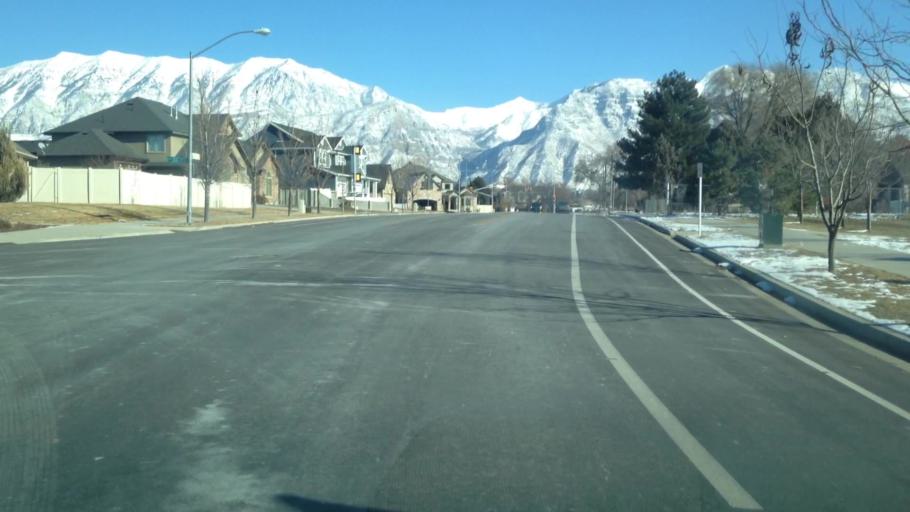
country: US
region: Utah
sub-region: Utah County
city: Orem
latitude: 40.2519
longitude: -111.7088
